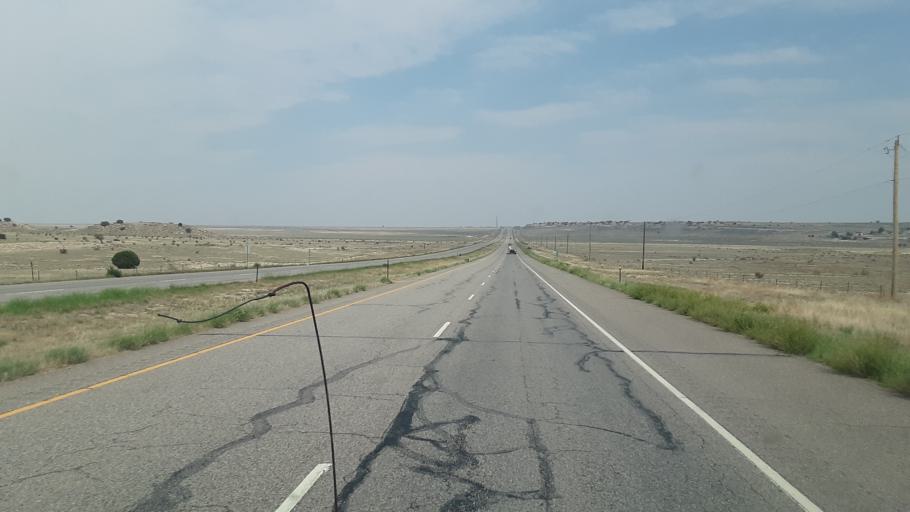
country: US
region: Colorado
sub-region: Pueblo County
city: Pueblo West
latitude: 38.3516
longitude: -104.8210
